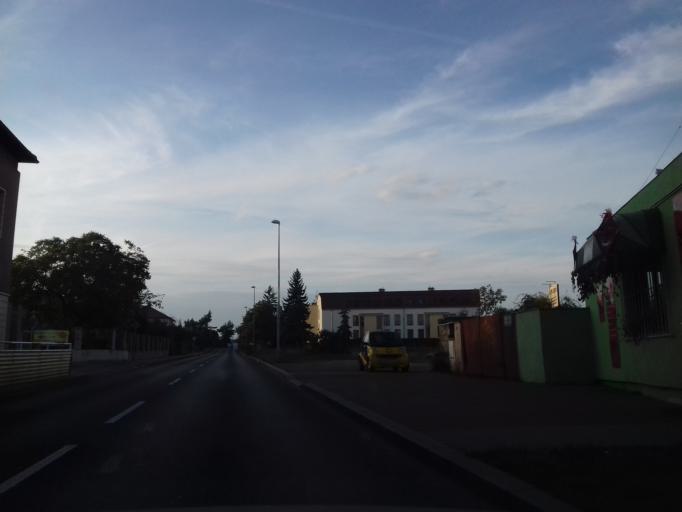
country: CZ
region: Praha
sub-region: Praha 4
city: Hodkovicky
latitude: 50.0141
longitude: 14.4570
